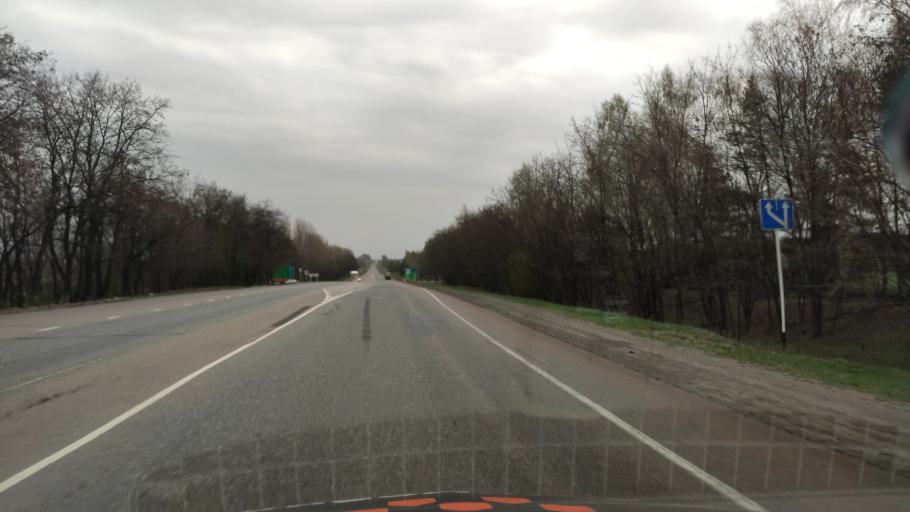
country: RU
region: Belgorod
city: Staryy Oskol
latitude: 51.4342
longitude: 37.9025
